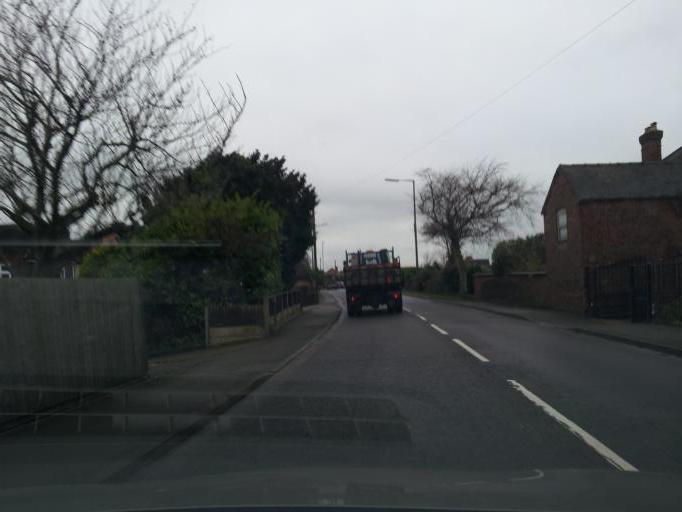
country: GB
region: England
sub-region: Derbyshire
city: Swadlincote
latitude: 52.7843
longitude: -1.5527
